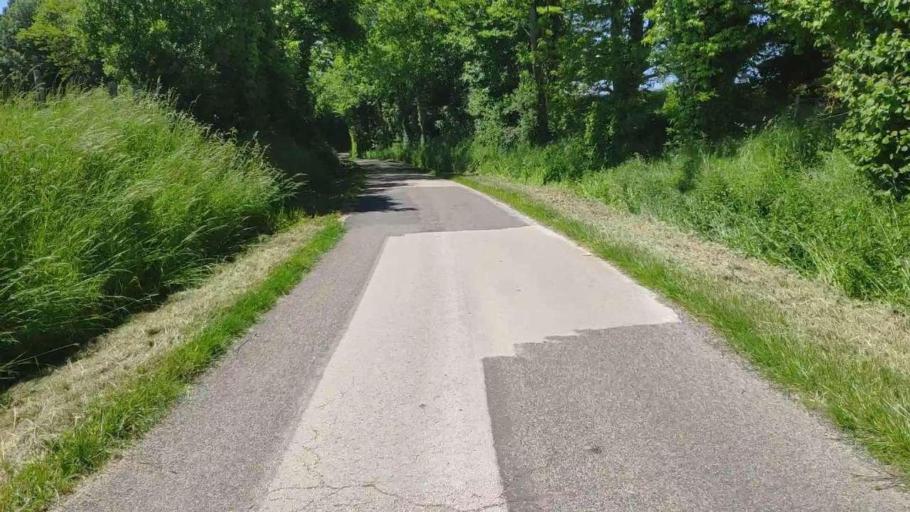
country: FR
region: Franche-Comte
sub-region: Departement du Jura
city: Bletterans
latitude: 46.7476
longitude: 5.3978
